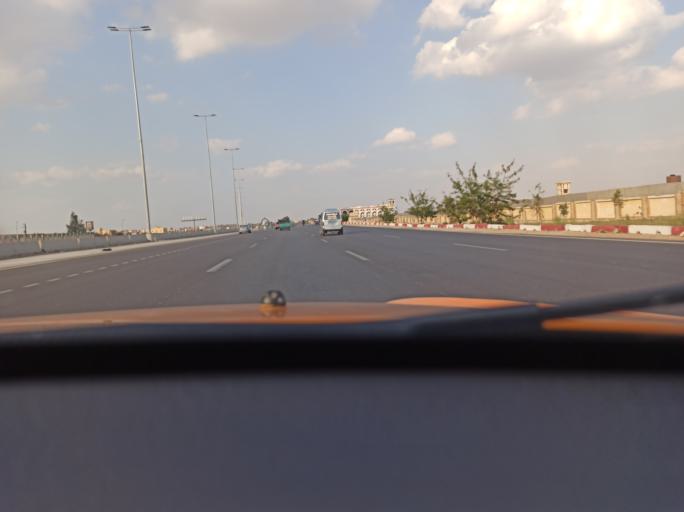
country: EG
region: Al Isma'iliyah
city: Ismailia
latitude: 30.6010
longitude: 32.2081
